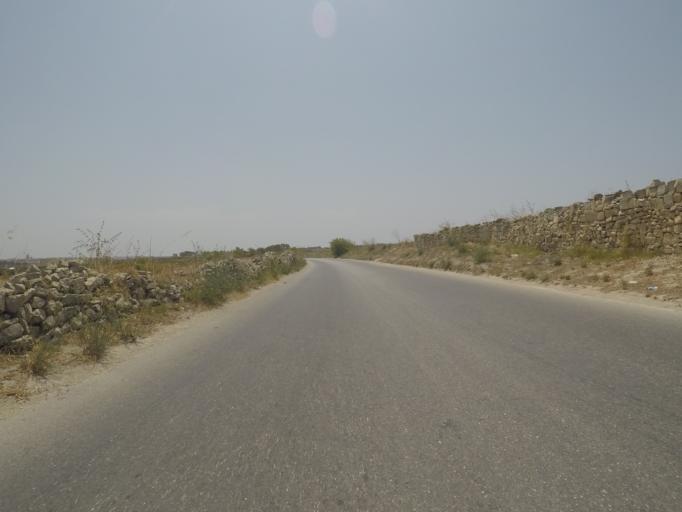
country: MT
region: Is-Siggiewi
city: Siggiewi
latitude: 35.8646
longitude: 14.4176
